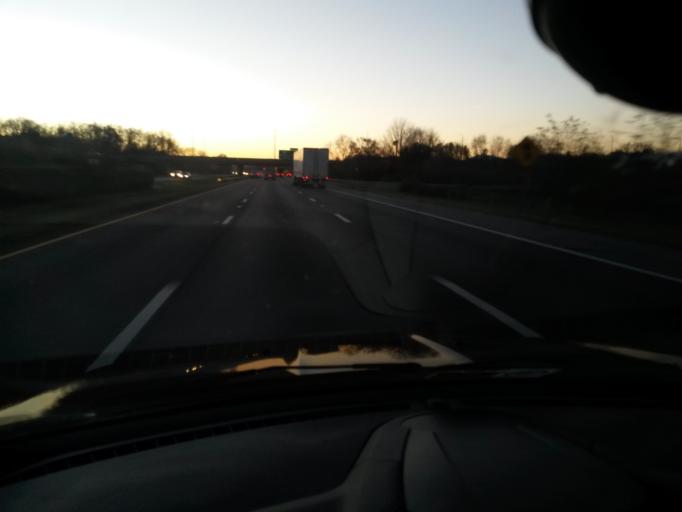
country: US
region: Virginia
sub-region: Roanoke County
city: Hollins
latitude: 37.3103
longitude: -79.9756
